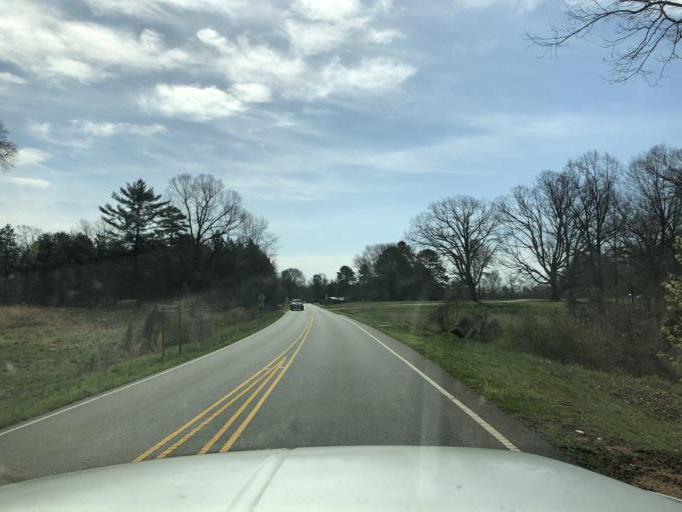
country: US
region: North Carolina
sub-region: Cleveland County
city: Shelby
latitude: 35.3859
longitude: -81.6221
